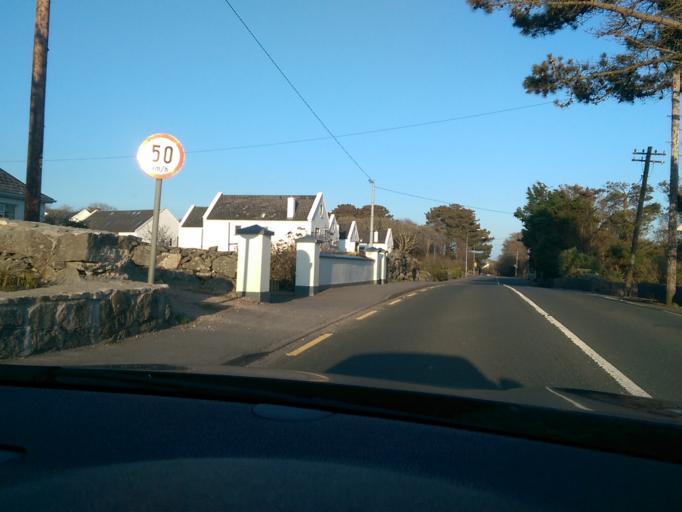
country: IE
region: Connaught
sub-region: County Galway
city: Moycullen
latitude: 53.2441
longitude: -9.3137
